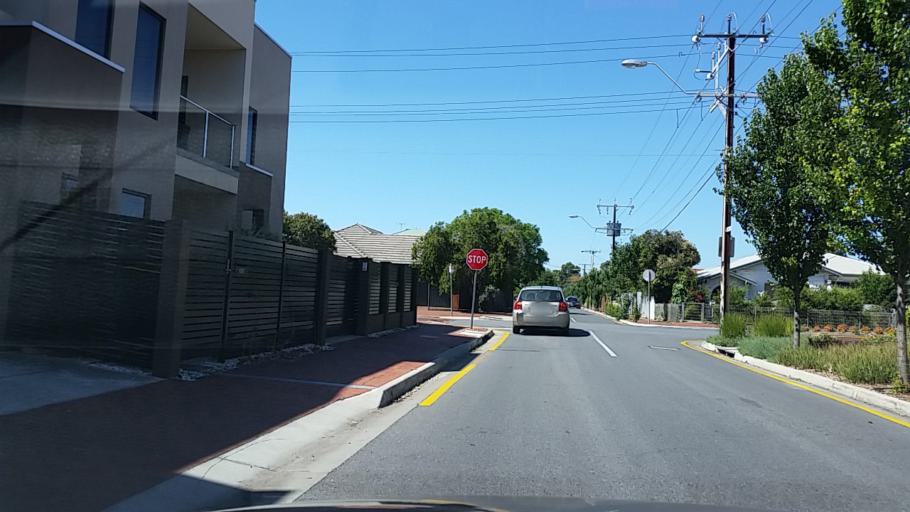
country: AU
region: South Australia
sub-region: Adelaide
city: North Adelaide
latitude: -34.8982
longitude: 138.5774
